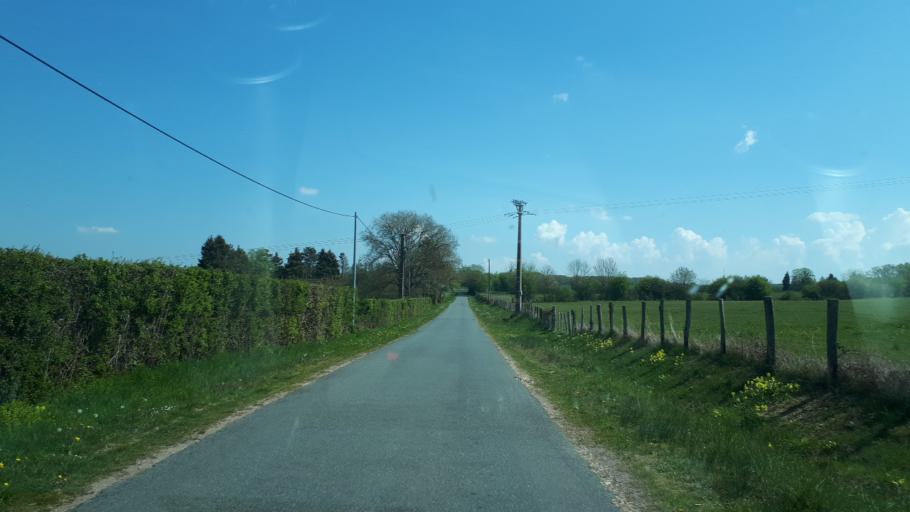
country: FR
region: Centre
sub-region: Departement du Cher
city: Henrichemont
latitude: 47.3026
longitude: 2.5367
